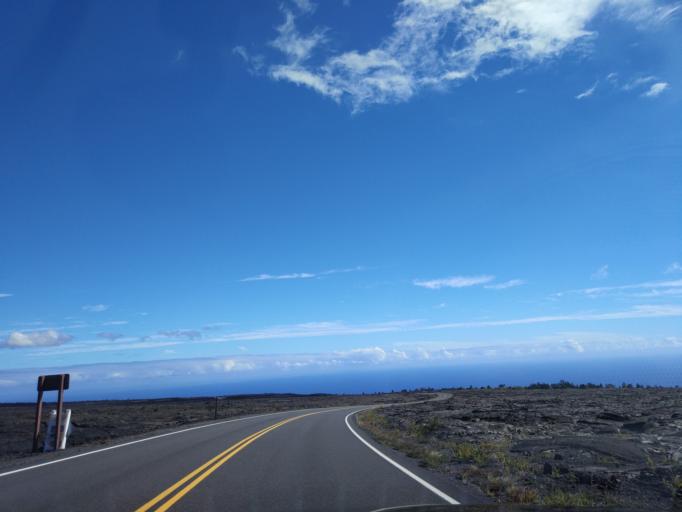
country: US
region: Hawaii
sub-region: Hawaii County
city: Volcano
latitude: 19.3363
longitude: -155.2031
